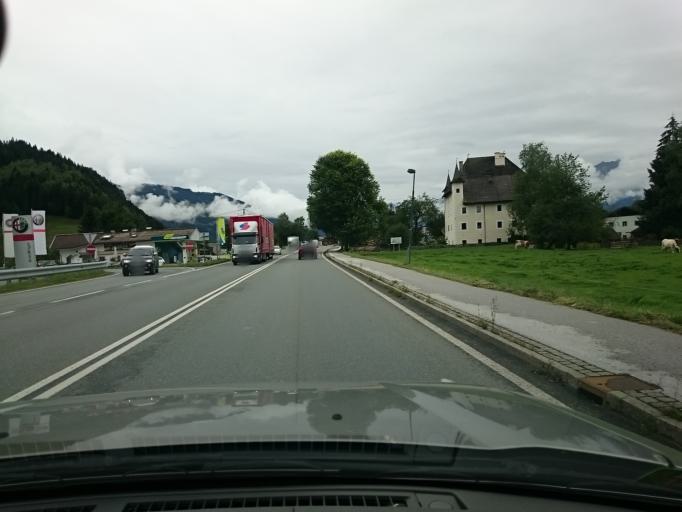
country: AT
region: Salzburg
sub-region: Politischer Bezirk Zell am See
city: Maishofen
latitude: 47.3586
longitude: 12.8000
